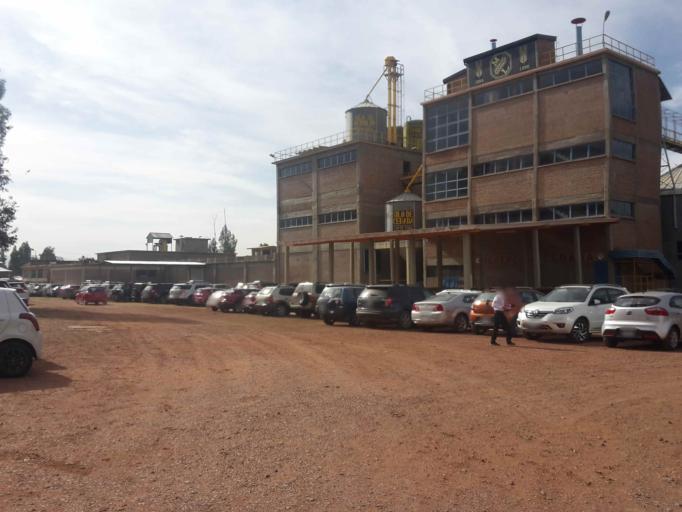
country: BO
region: Cochabamba
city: Cochabamba
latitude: -17.3554
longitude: -66.2016
